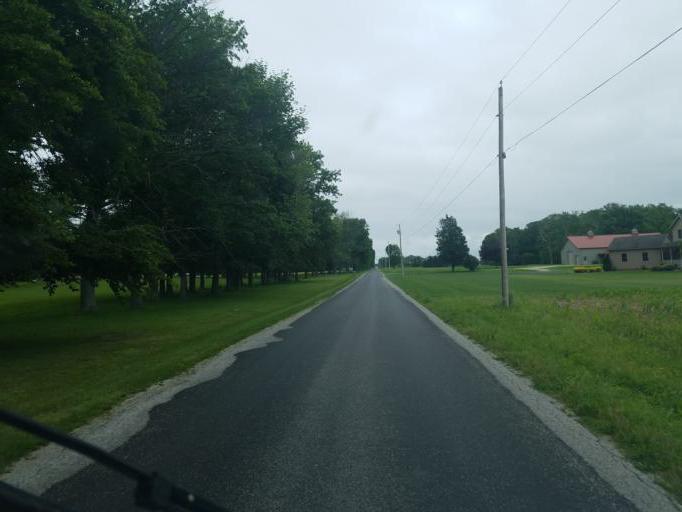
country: US
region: Ohio
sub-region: Marion County
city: Marion
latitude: 40.5055
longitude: -83.0512
